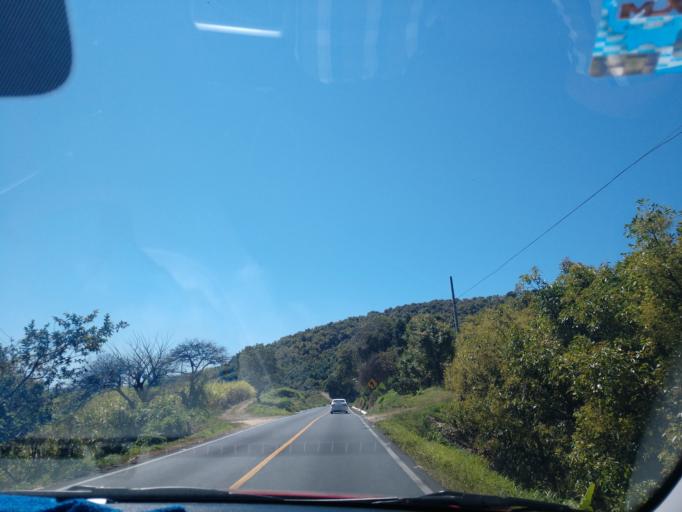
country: MX
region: Nayarit
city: Xalisco
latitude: 21.3975
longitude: -104.8959
